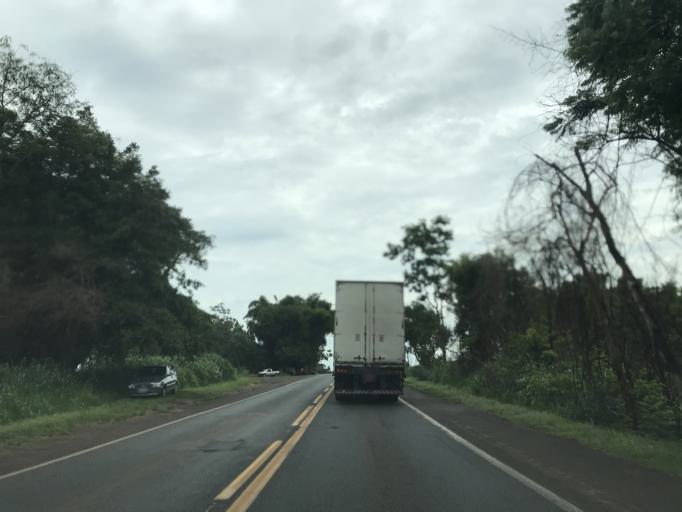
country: BR
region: Minas Gerais
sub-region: Frutal
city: Frutal
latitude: -20.1867
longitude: -49.1184
